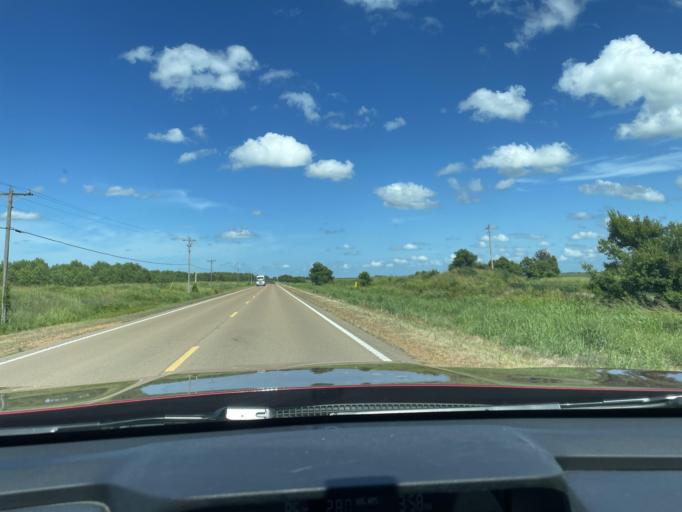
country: US
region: Mississippi
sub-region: Humphreys County
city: Belzoni
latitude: 33.1834
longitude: -90.5995
